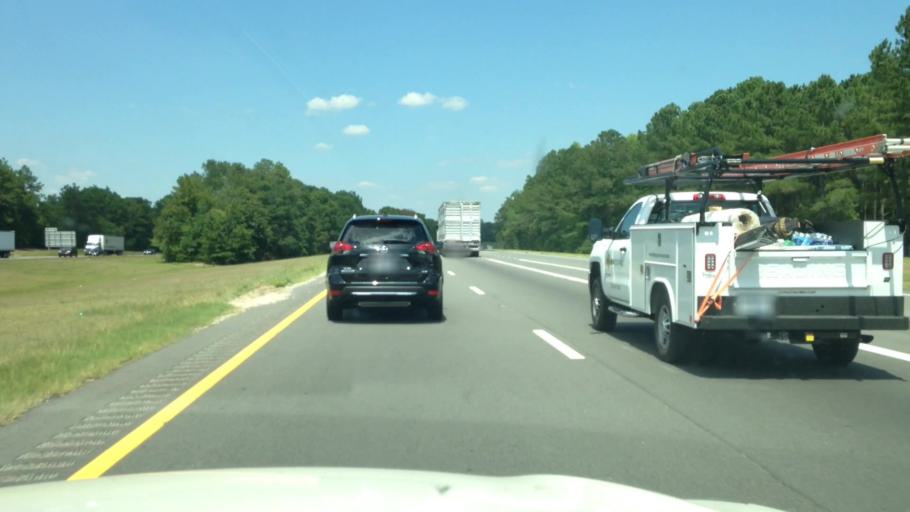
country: US
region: North Carolina
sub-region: Cumberland County
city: Hope Mills
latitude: 34.9640
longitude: -78.8868
